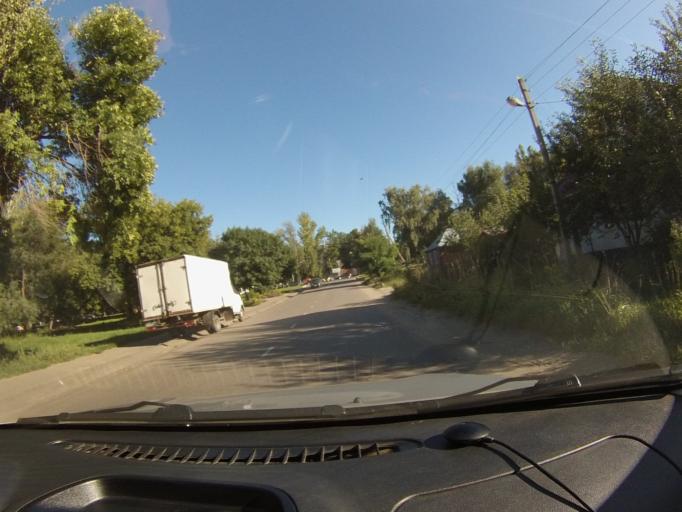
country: RU
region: Tambov
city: Tambov
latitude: 52.7550
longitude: 41.4263
